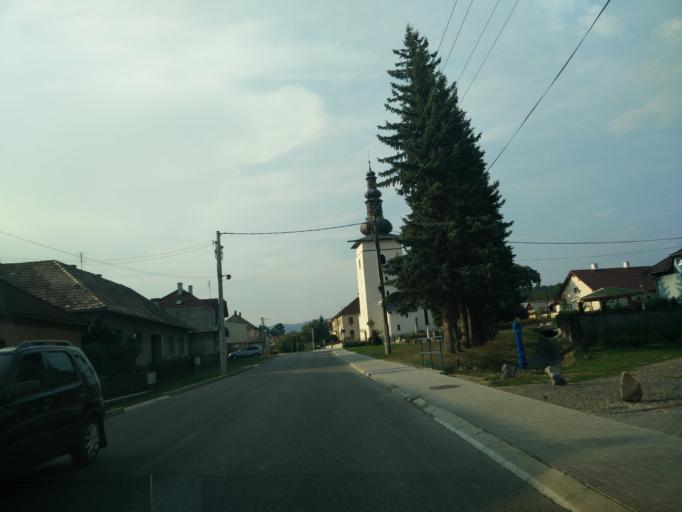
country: SK
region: Banskobystricky
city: Ziar nad Hronom
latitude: 48.6155
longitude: 18.8416
